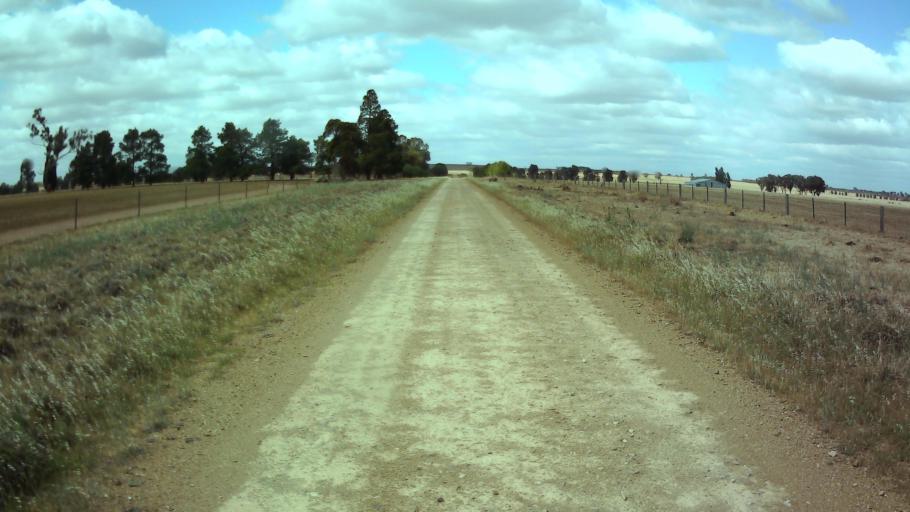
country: AU
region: New South Wales
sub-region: Weddin
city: Grenfell
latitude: -34.0581
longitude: 148.3307
